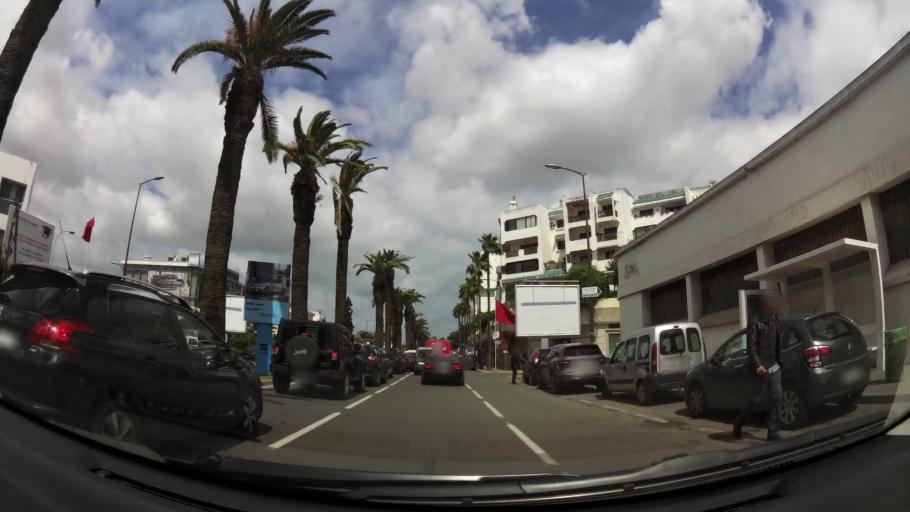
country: MA
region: Grand Casablanca
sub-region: Casablanca
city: Casablanca
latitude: 33.5755
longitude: -7.6517
